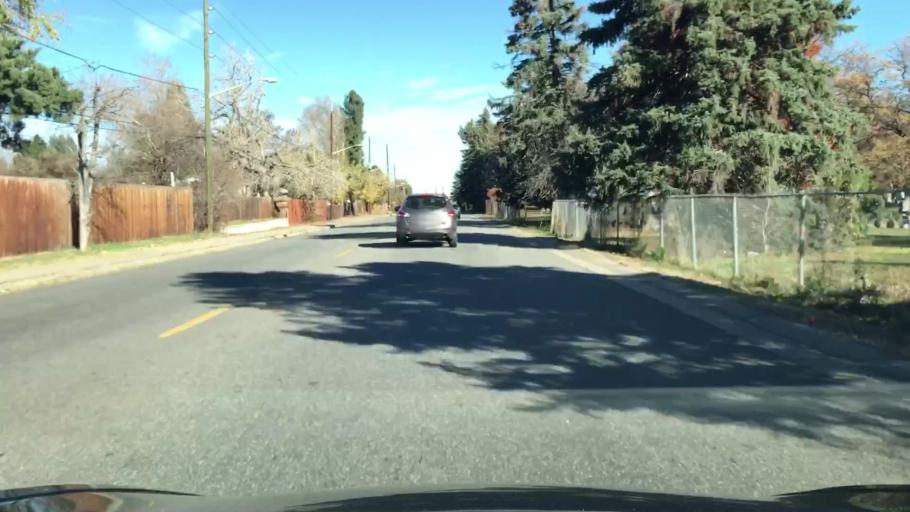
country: US
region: Colorado
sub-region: Arapahoe County
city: Glendale
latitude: 39.7054
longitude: -104.9034
